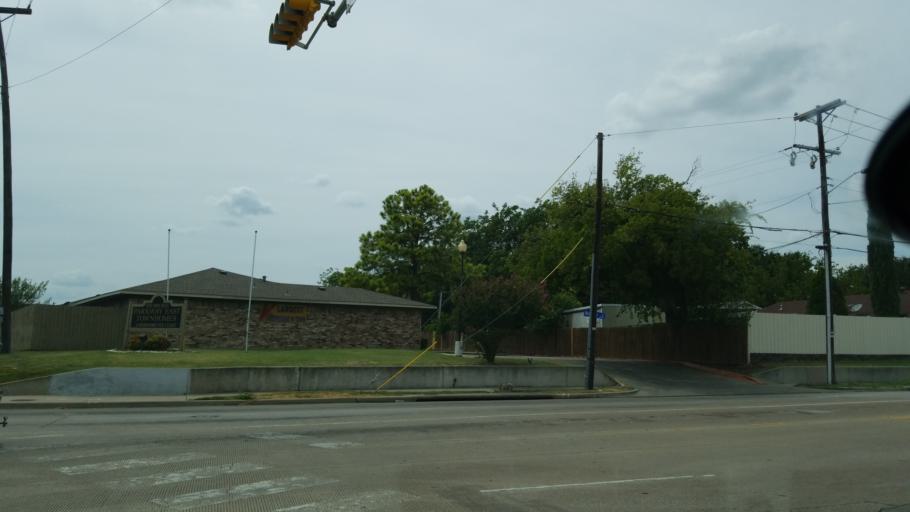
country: US
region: Texas
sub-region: Tarrant County
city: Arlington
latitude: 32.7091
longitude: -97.0853
